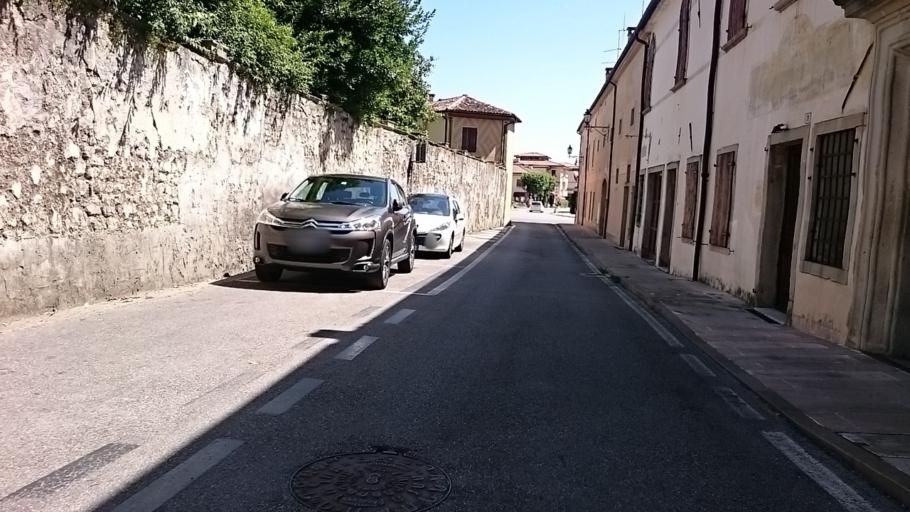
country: IT
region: Veneto
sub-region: Provincia di Treviso
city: Follina
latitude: 45.9536
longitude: 12.1177
